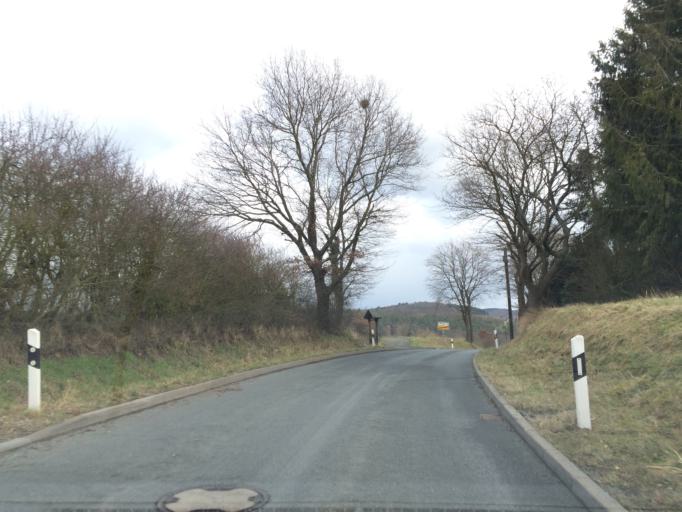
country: DE
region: Hesse
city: Weilmunster
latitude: 50.3823
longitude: 8.4020
